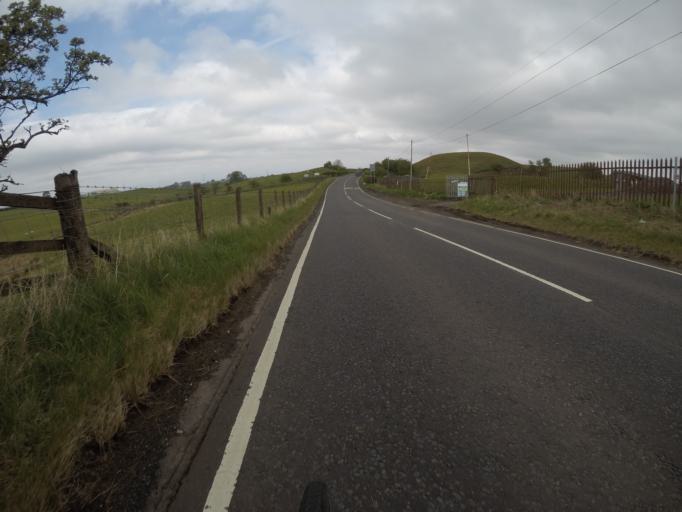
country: GB
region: Scotland
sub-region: East Renfrewshire
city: Barrhead
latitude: 55.7549
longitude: -4.3840
